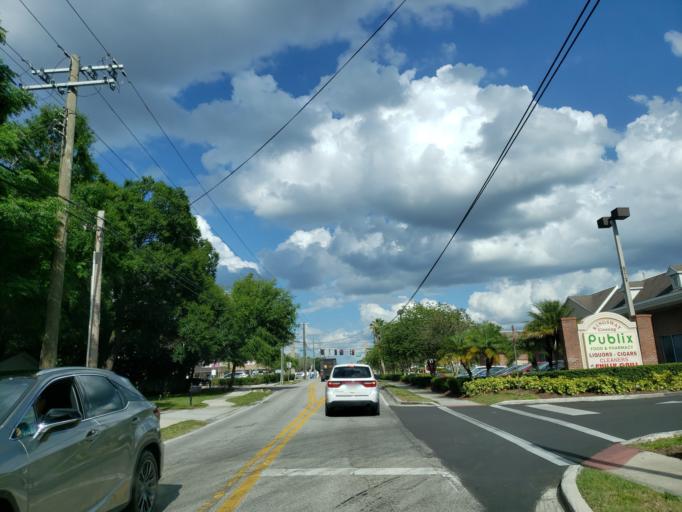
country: US
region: Florida
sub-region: Hillsborough County
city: Brandon
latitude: 27.9596
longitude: -82.2790
